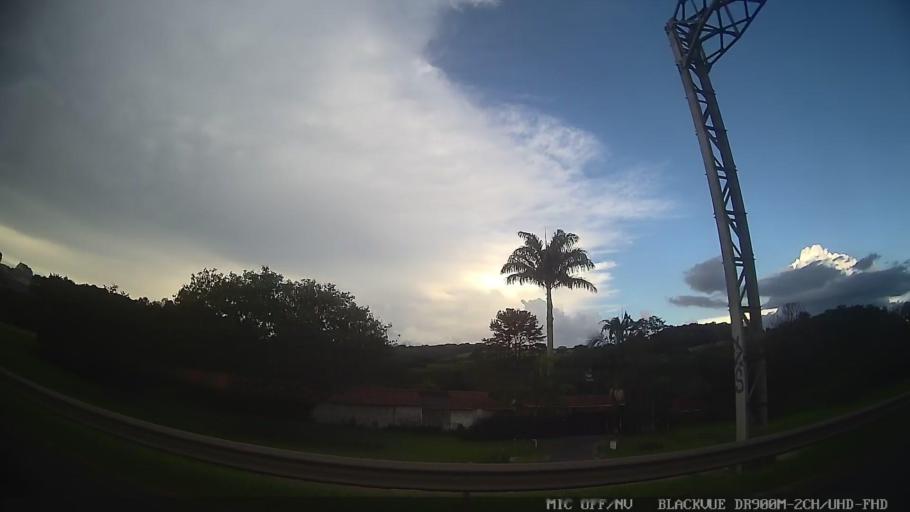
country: BR
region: Sao Paulo
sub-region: Atibaia
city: Atibaia
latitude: -23.1003
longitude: -46.5370
